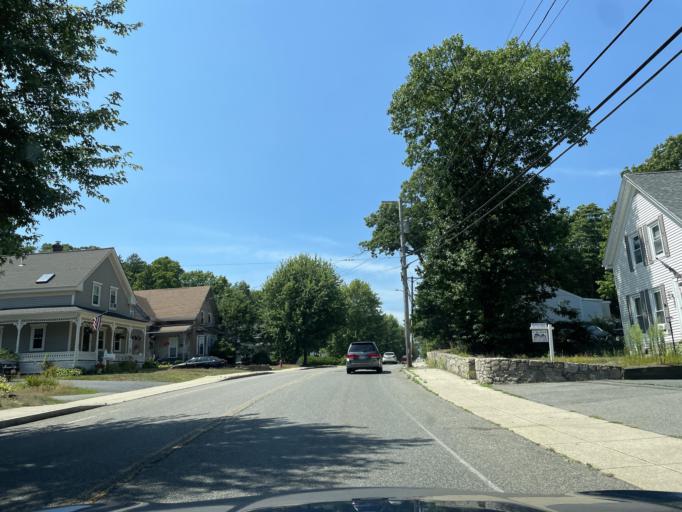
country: US
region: Massachusetts
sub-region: Norfolk County
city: Randolph
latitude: 42.1579
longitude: -71.0337
